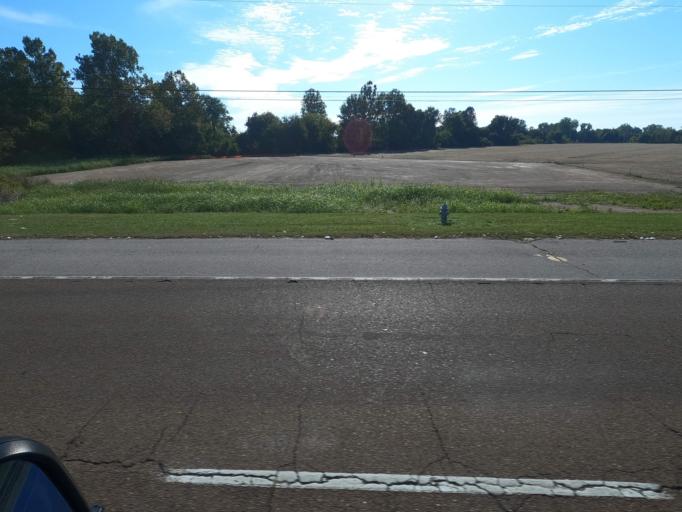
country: US
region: Tennessee
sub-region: Shelby County
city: Millington
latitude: 35.3652
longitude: -89.8883
